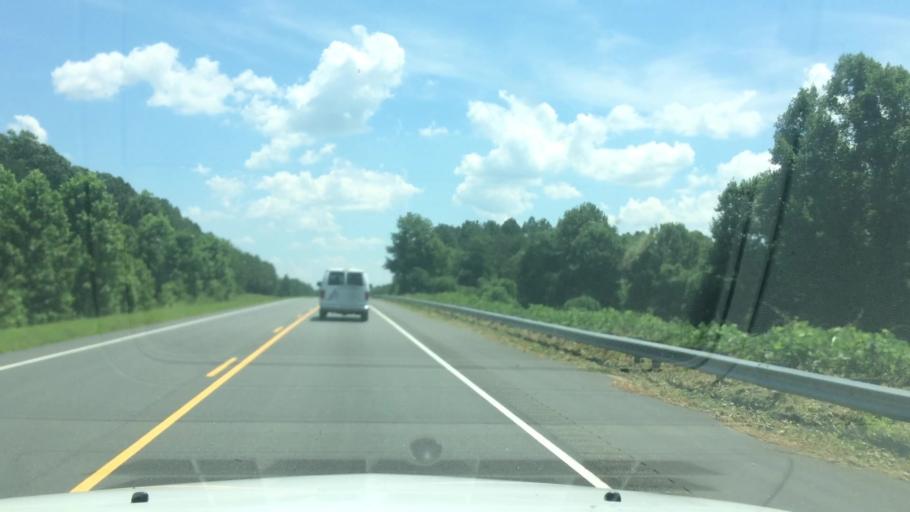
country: US
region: North Carolina
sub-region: Alexander County
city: Stony Point
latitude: 35.8111
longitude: -80.9748
